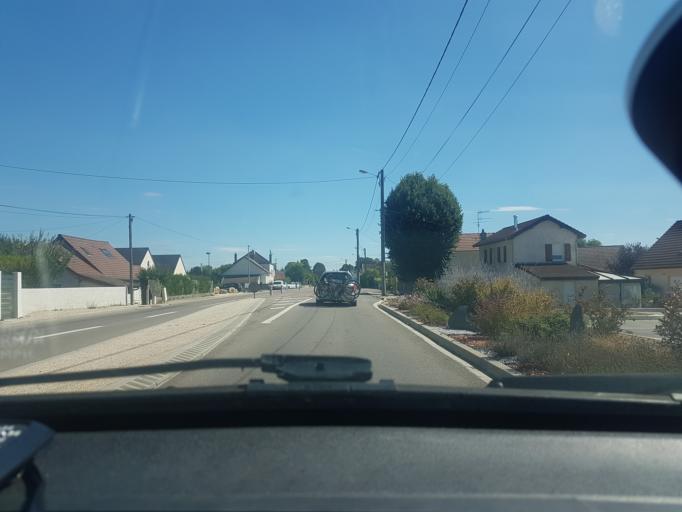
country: FR
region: Bourgogne
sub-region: Departement de la Cote-d'Or
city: Arc-sur-Tille
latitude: 47.3480
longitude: 5.1817
